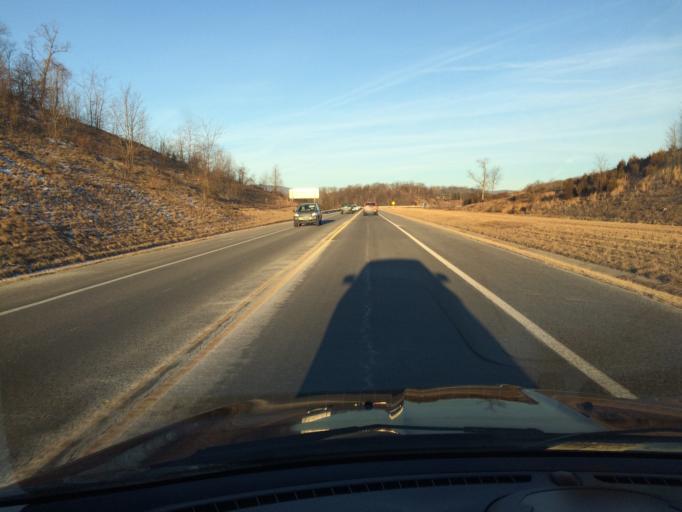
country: US
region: Virginia
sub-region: City of Staunton
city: Staunton
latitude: 38.1388
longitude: -79.1063
